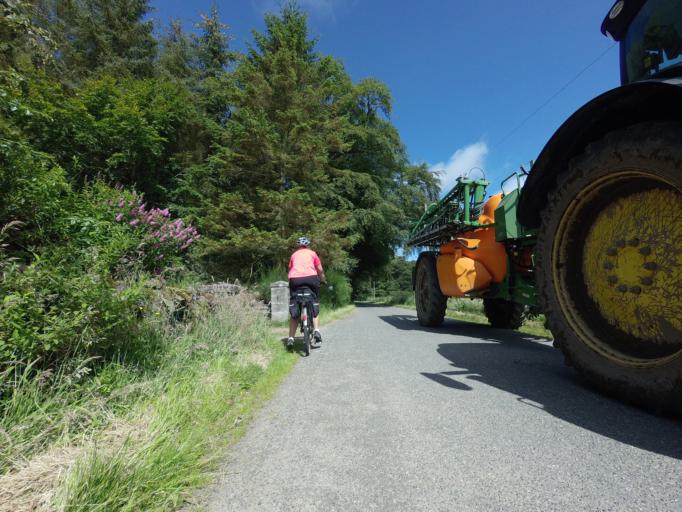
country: GB
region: Scotland
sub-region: Aberdeenshire
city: Turriff
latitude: 57.5871
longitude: -2.5050
